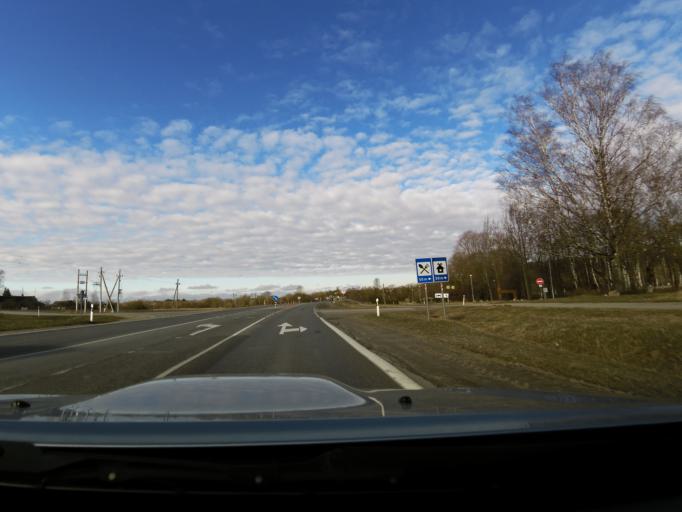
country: LT
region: Panevezys
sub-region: Panevezys City
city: Panevezys
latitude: 55.7344
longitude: 24.2424
